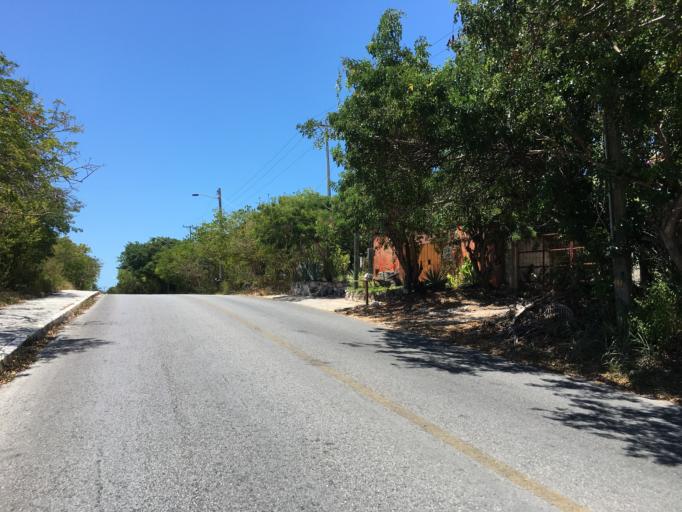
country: MX
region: Quintana Roo
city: Isla Mujeres
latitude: 21.2124
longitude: -86.7224
